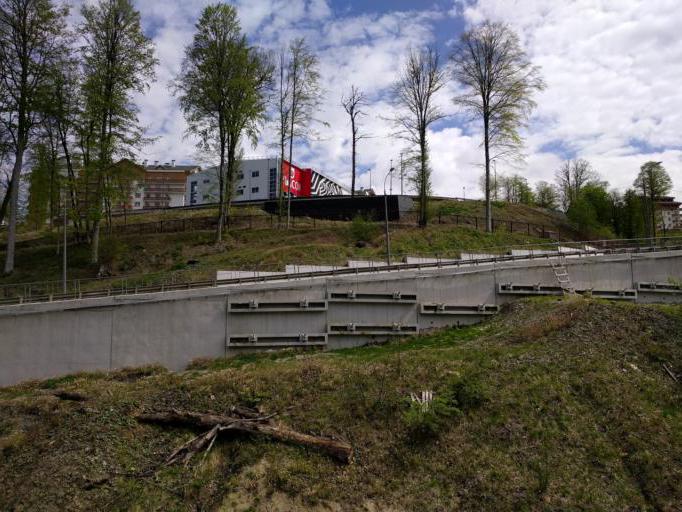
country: RU
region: Krasnodarskiy
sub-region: Sochi City
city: Krasnaya Polyana
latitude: 43.6620
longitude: 40.3136
